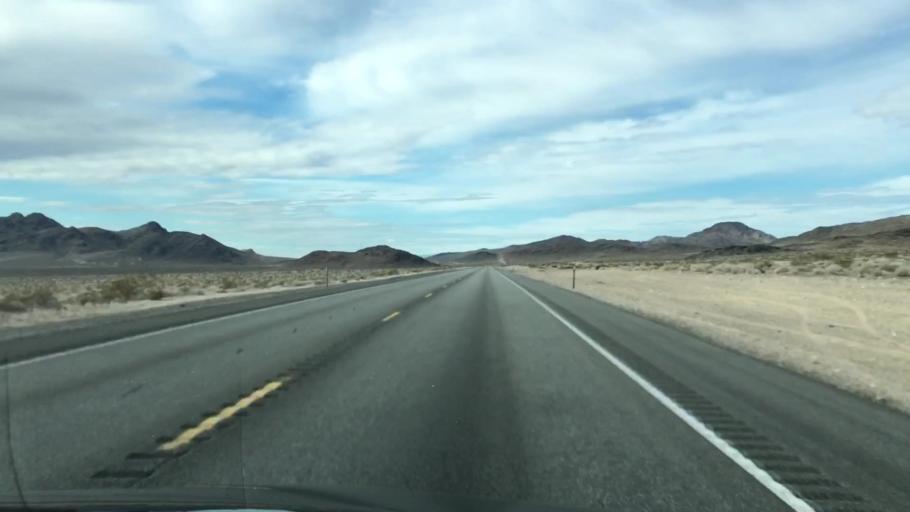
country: US
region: Nevada
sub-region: Nye County
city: Pahrump
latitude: 36.6173
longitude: -116.2862
